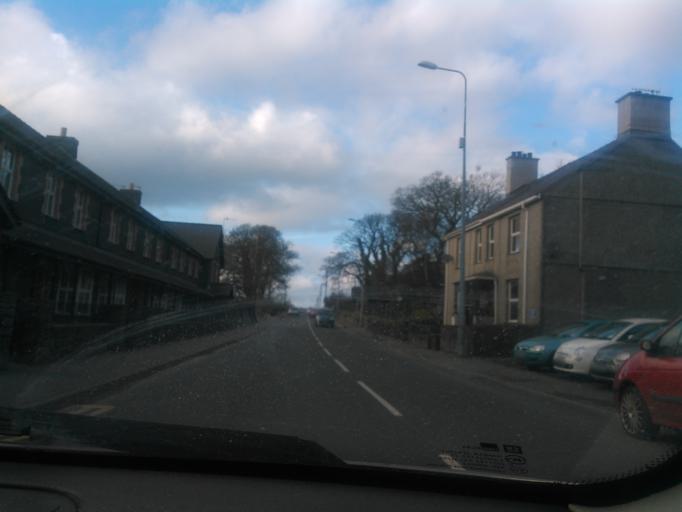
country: GB
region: Wales
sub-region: Gwynedd
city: Bethesda
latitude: 53.1822
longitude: -4.0681
